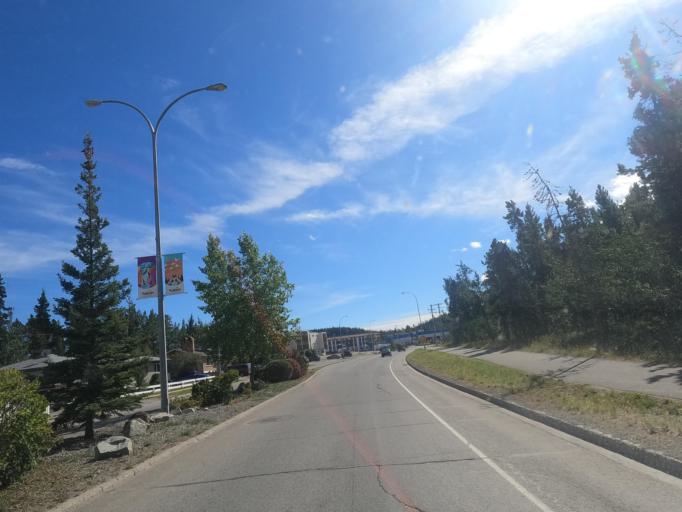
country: CA
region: Yukon
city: Whitehorse
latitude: 60.7077
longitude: -135.0351
